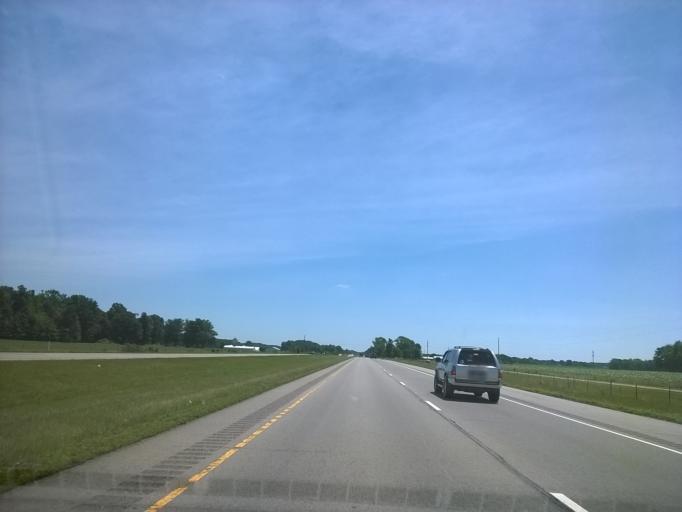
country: US
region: Indiana
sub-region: Ripley County
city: Sunman
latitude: 39.2856
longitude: -85.0635
